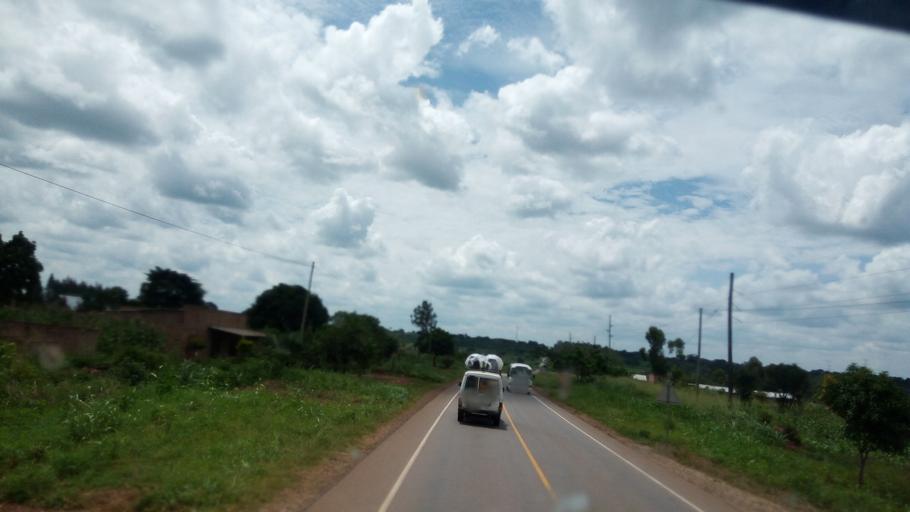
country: UG
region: Western Region
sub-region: Kiryandongo District
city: Kiryandongo
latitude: 1.8647
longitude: 32.0490
